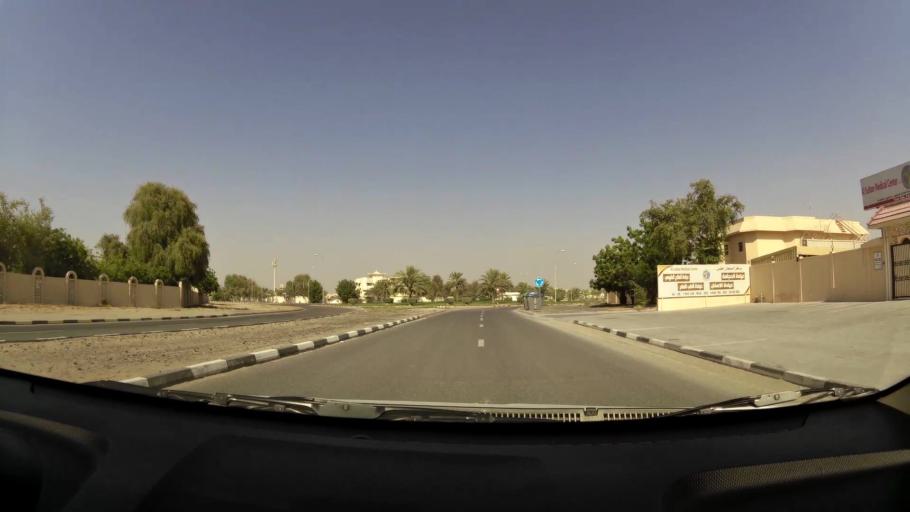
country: AE
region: Ajman
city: Ajman
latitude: 25.4087
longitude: 55.4644
